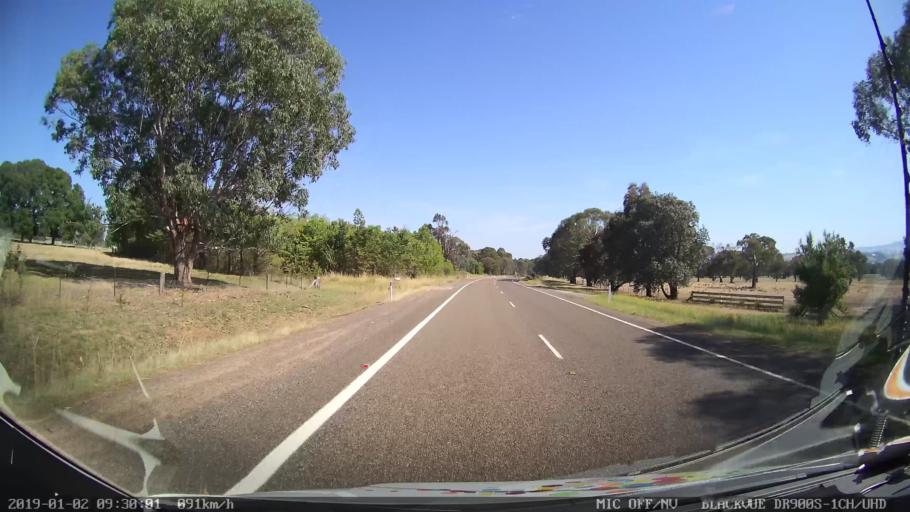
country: AU
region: New South Wales
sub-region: Tumut Shire
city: Tumut
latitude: -35.3318
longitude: 148.2381
